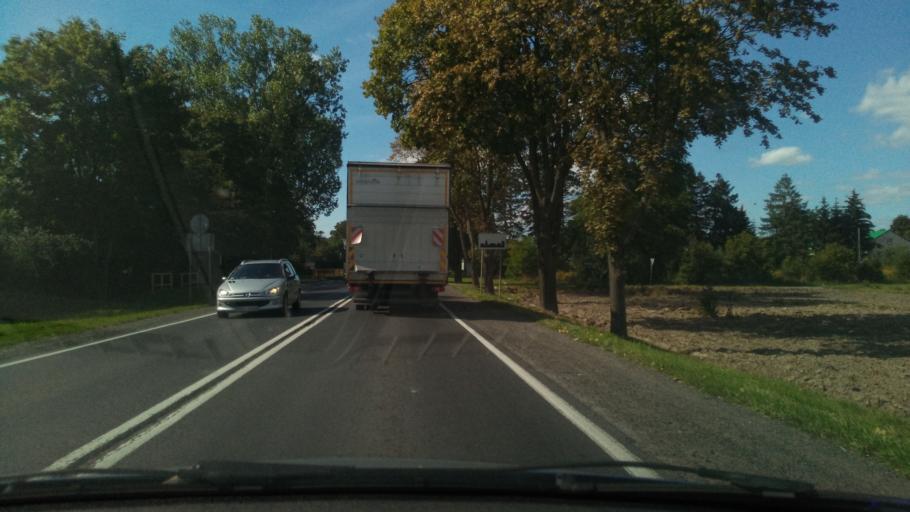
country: PL
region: Lodz Voivodeship
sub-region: Piotrkow Trybunalski
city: Piotrkow Trybunalski
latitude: 51.3921
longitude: 19.7703
